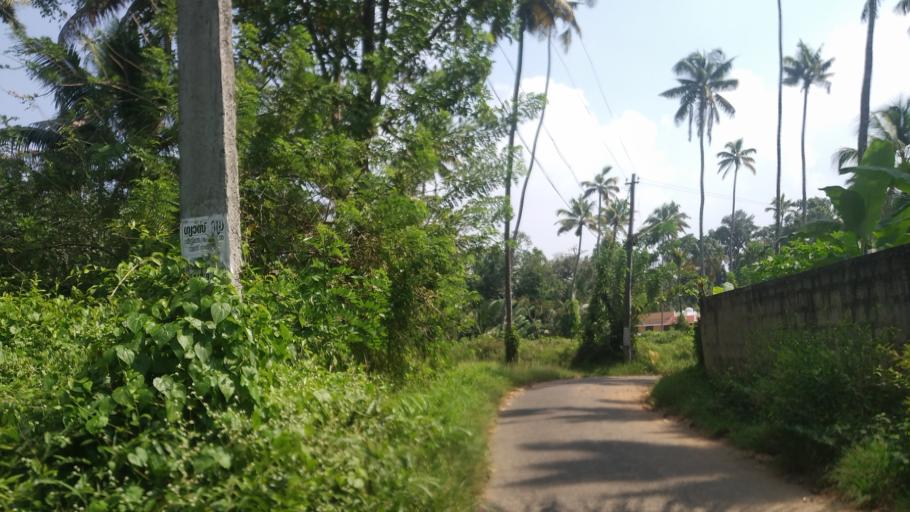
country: IN
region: Kerala
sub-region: Ernakulam
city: Elur
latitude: 10.1266
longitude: 76.2335
